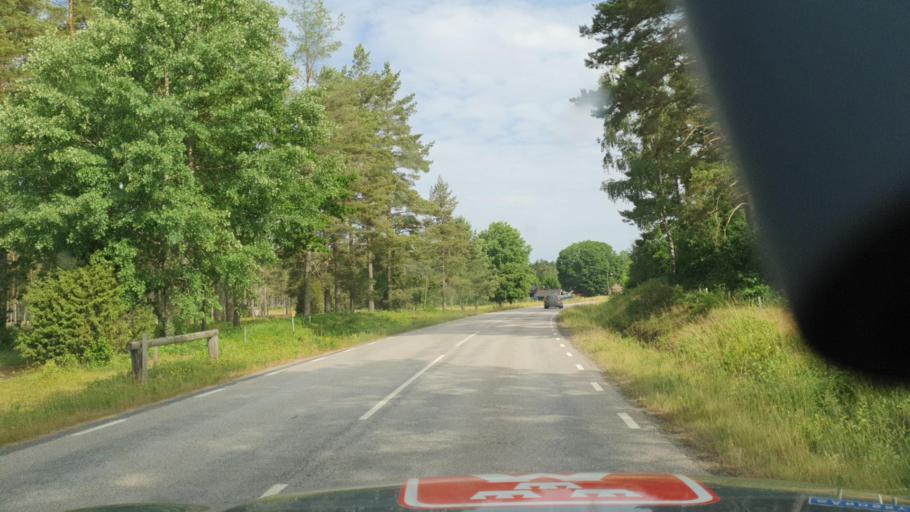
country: SE
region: Kalmar
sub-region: Nybro Kommun
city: Nybro
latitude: 56.6926
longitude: 15.9821
